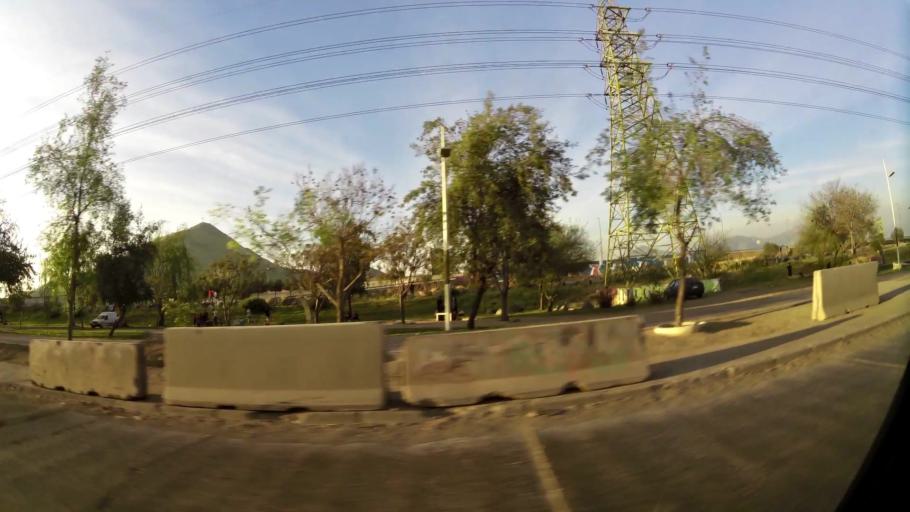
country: CL
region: Santiago Metropolitan
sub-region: Provincia de Santiago
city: Lo Prado
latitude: -33.4089
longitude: -70.7043
